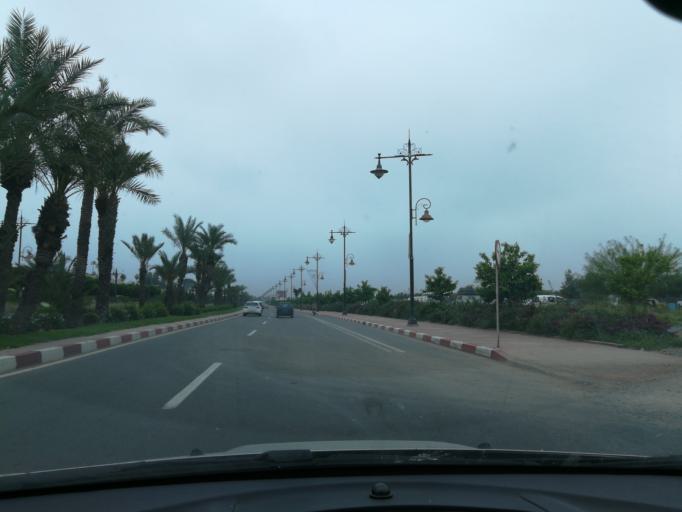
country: MA
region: Marrakech-Tensift-Al Haouz
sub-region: Marrakech
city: Marrakesh
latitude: 31.6209
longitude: -7.9989
